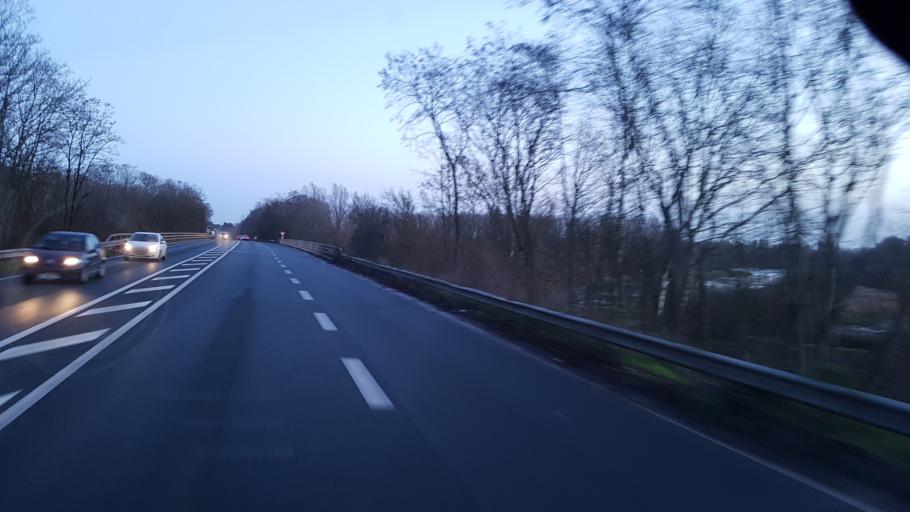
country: FR
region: Nord-Pas-de-Calais
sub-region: Departement du Nord
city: Lambres-lez-Douai
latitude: 50.3547
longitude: 3.0507
